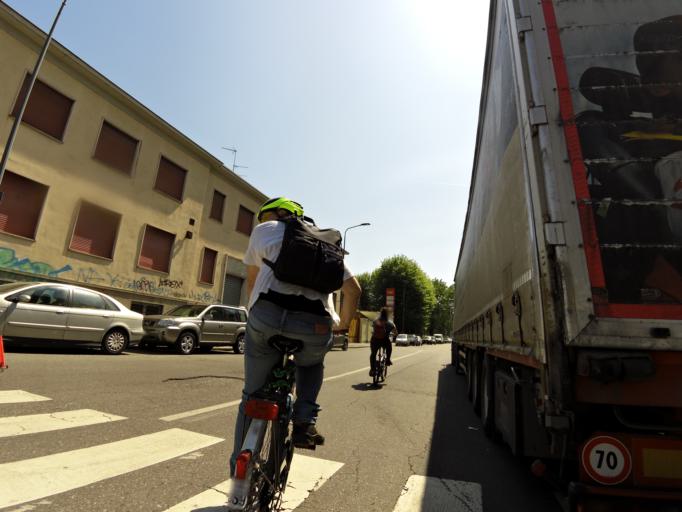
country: IT
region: Lombardy
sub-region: Citta metropolitana di Milano
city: Sesto San Giovanni
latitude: 45.5021
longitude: 9.2281
